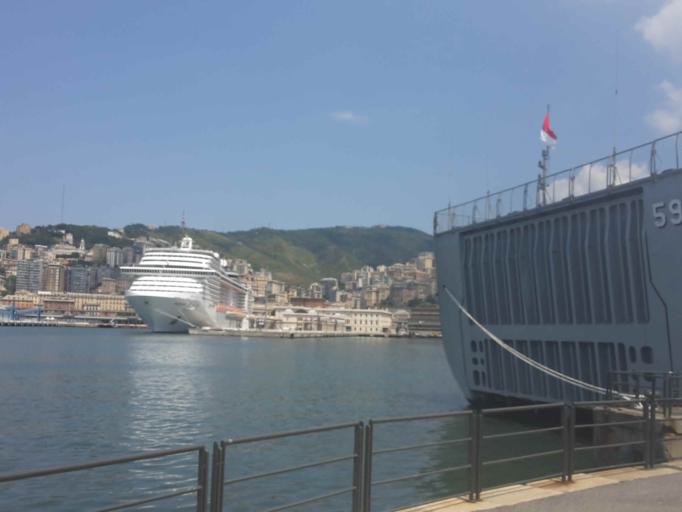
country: IT
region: Liguria
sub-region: Provincia di Genova
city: San Teodoro
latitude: 44.4078
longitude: 8.9187
